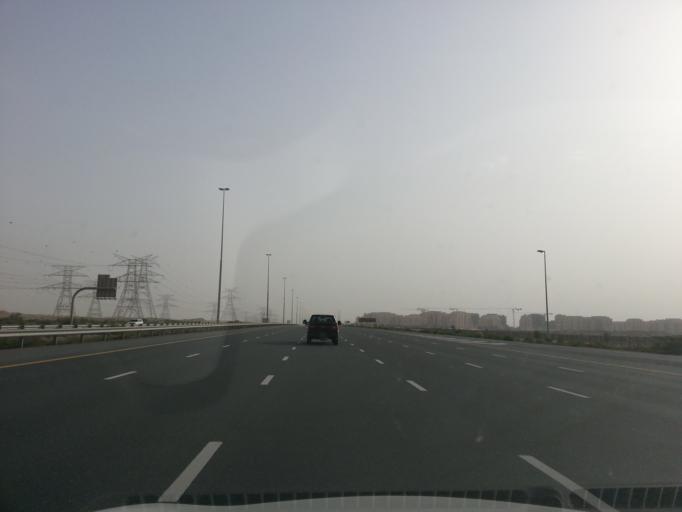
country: AE
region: Dubai
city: Dubai
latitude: 25.0082
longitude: 55.2660
